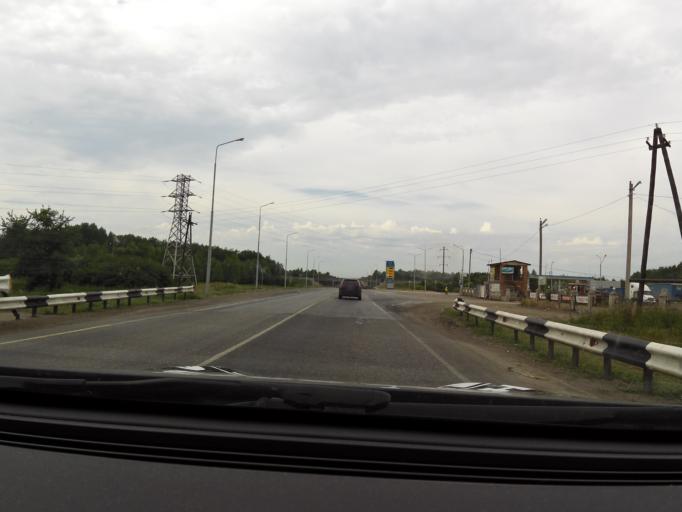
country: RU
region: Bashkortostan
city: Iglino
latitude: 54.7442
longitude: 56.3095
